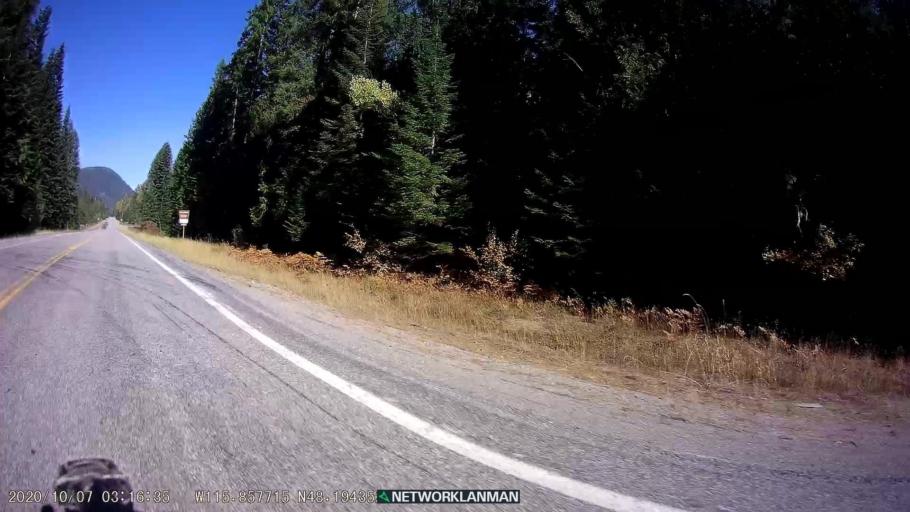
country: US
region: Montana
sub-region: Lincoln County
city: Libby
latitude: 48.1948
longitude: -115.8577
